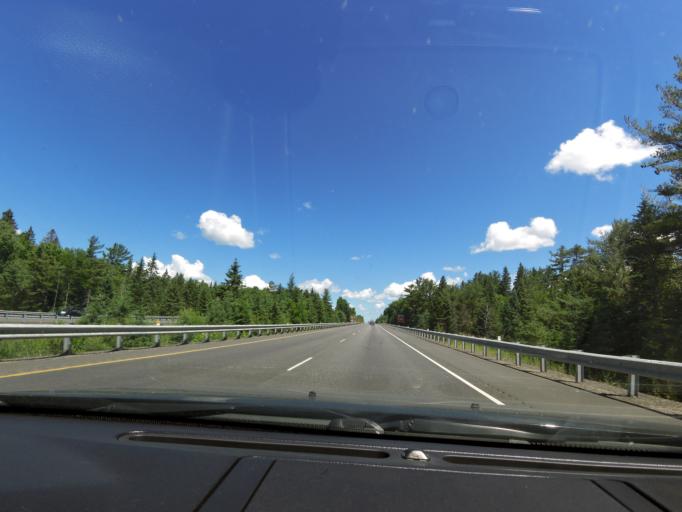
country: CA
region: Ontario
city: Bracebridge
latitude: 45.1682
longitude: -79.3115
